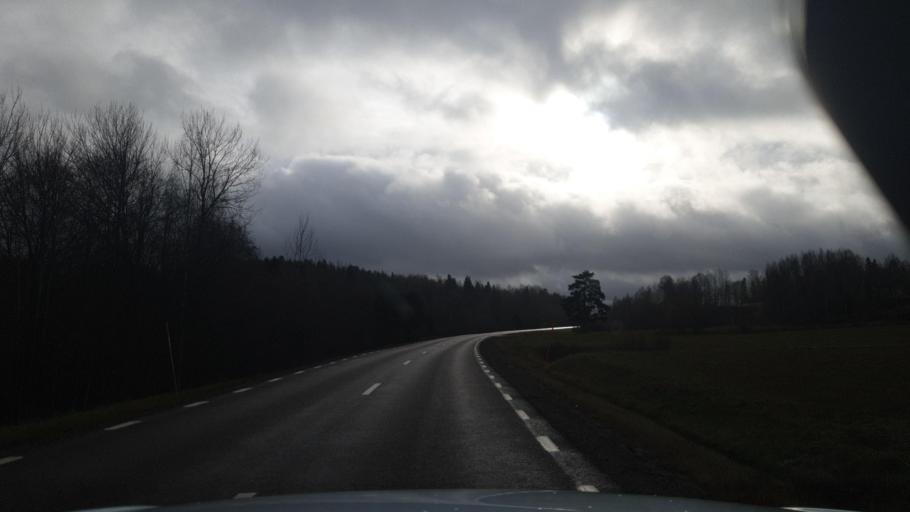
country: SE
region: Vaermland
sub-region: Arjangs Kommun
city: Arjaeng
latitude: 59.6316
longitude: 12.1409
